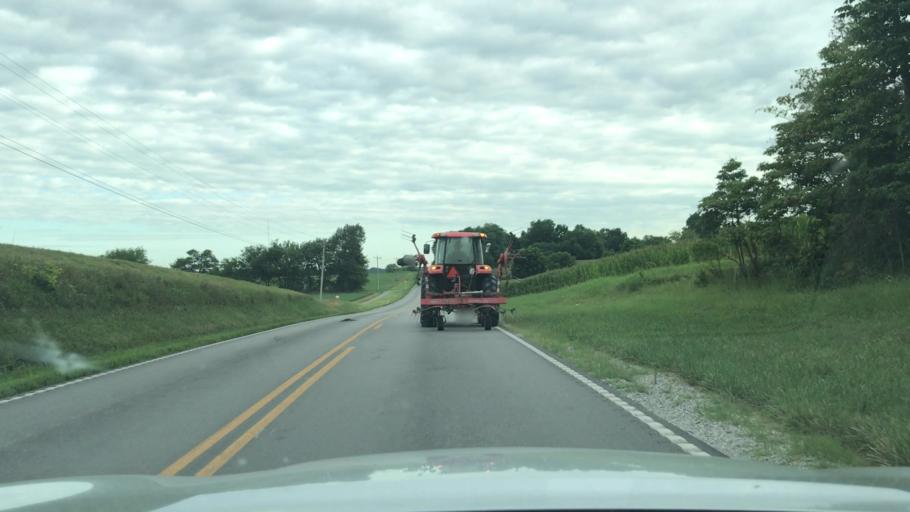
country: US
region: Kentucky
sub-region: Todd County
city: Guthrie
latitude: 36.6877
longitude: -87.2010
